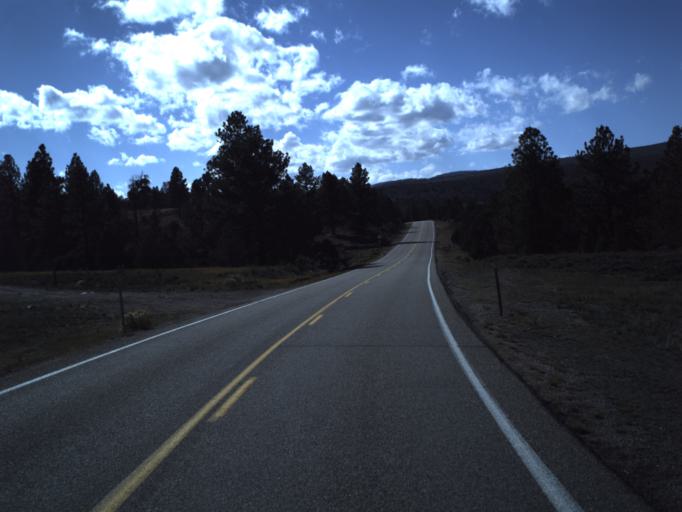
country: US
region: Utah
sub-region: Garfield County
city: Panguitch
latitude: 37.7485
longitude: -112.5715
